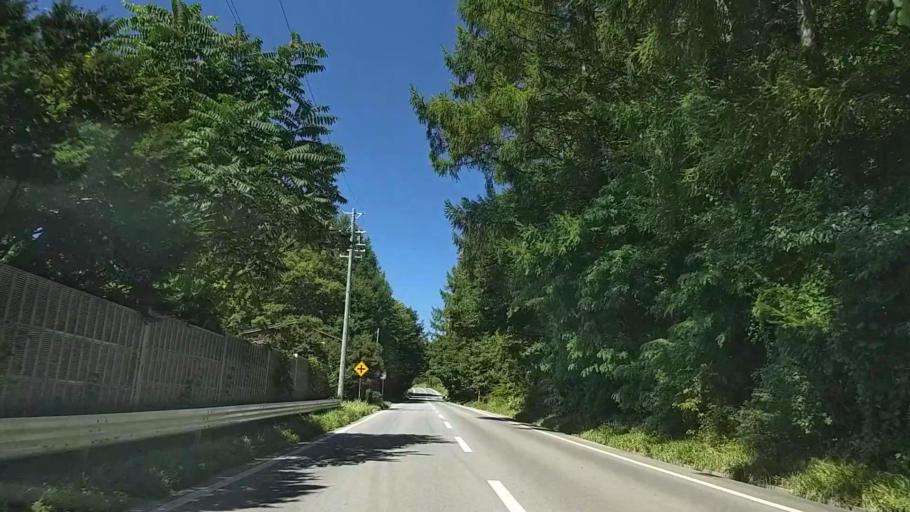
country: JP
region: Nagano
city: Komoro
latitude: 36.3408
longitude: 138.4977
